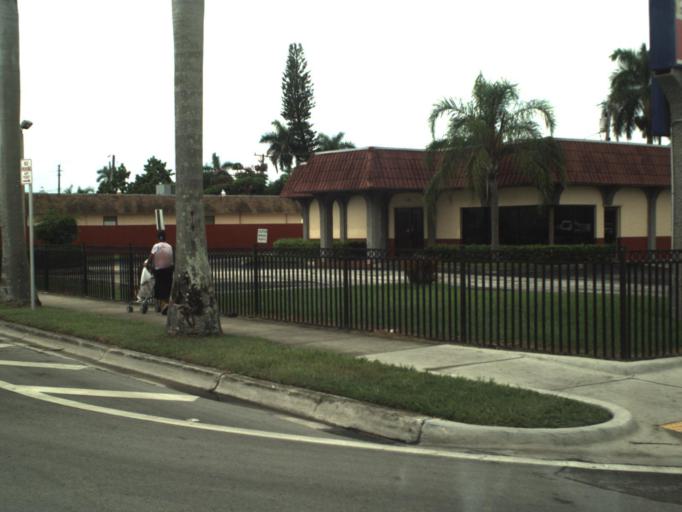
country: US
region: Florida
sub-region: Miami-Dade County
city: Homestead
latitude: 25.4753
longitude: -80.4775
